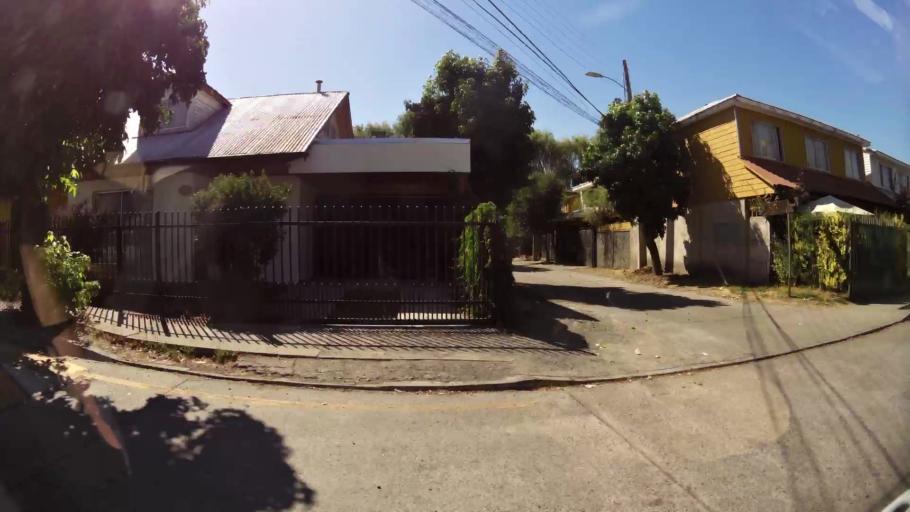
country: CL
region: Maule
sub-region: Provincia de Curico
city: Curico
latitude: -34.9746
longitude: -71.2616
